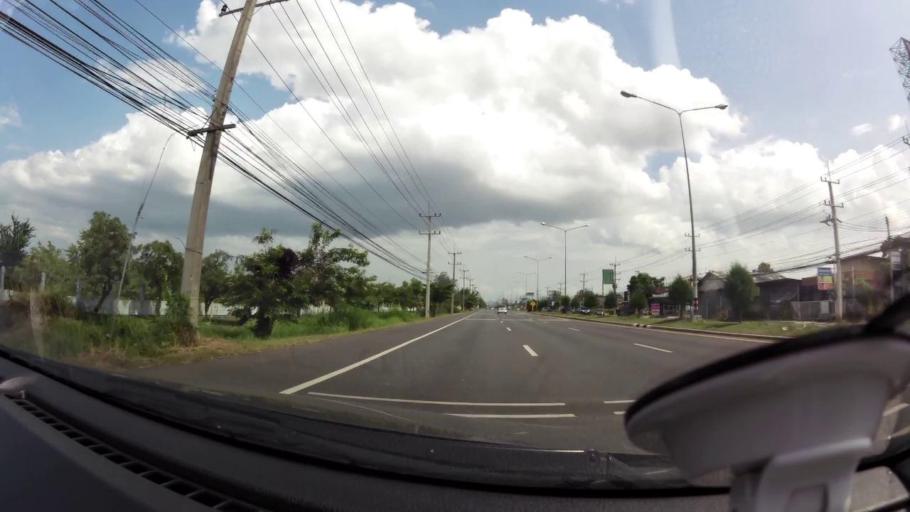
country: TH
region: Prachuap Khiri Khan
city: Hua Hin
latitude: 12.6810
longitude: 99.9528
